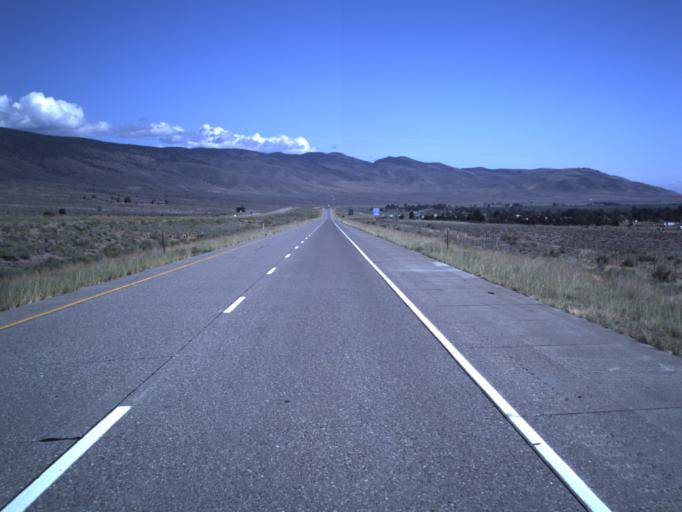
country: US
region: Utah
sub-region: Sevier County
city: Monroe
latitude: 38.6129
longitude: -112.2308
